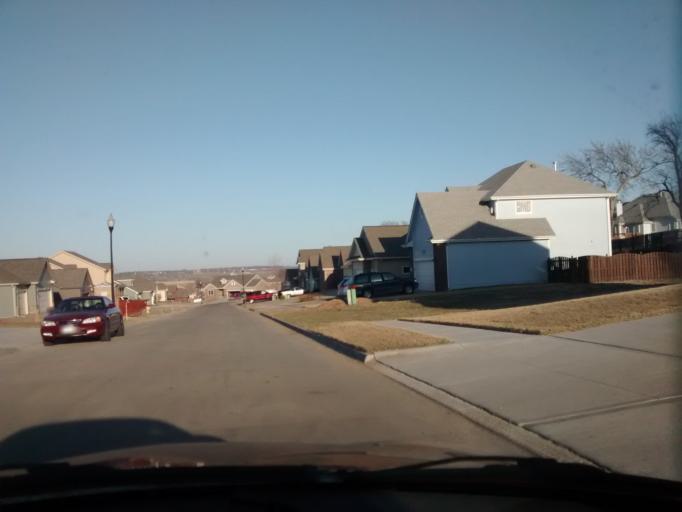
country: US
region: Nebraska
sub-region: Sarpy County
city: Papillion
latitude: 41.1434
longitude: -95.9844
